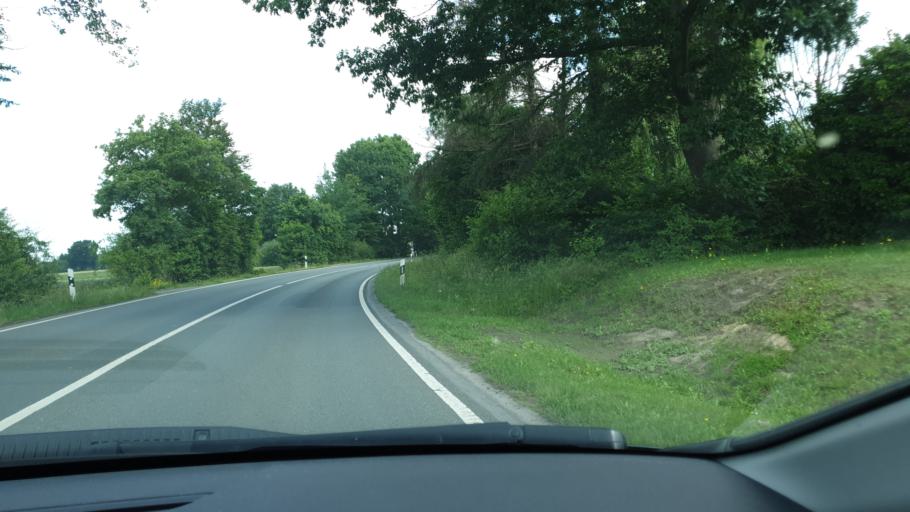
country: DE
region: North Rhine-Westphalia
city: Rietberg
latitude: 51.7977
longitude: 8.4191
